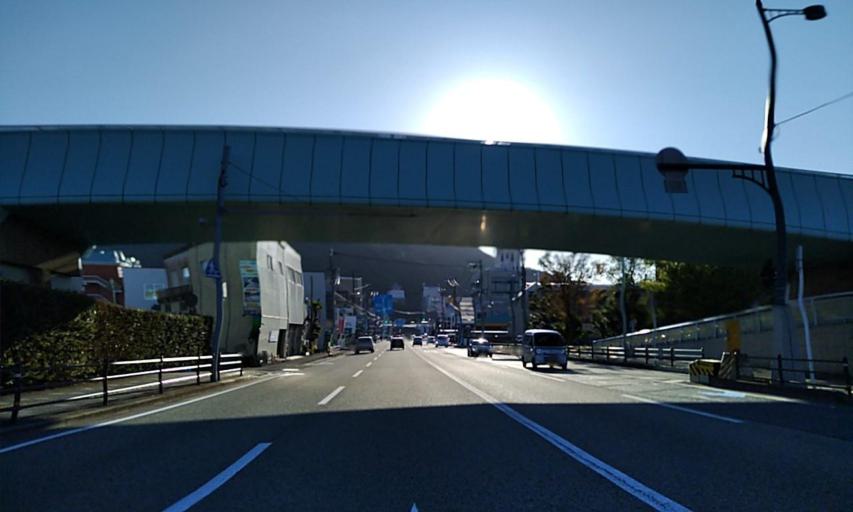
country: JP
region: Wakayama
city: Kainan
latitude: 34.1867
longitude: 135.1819
